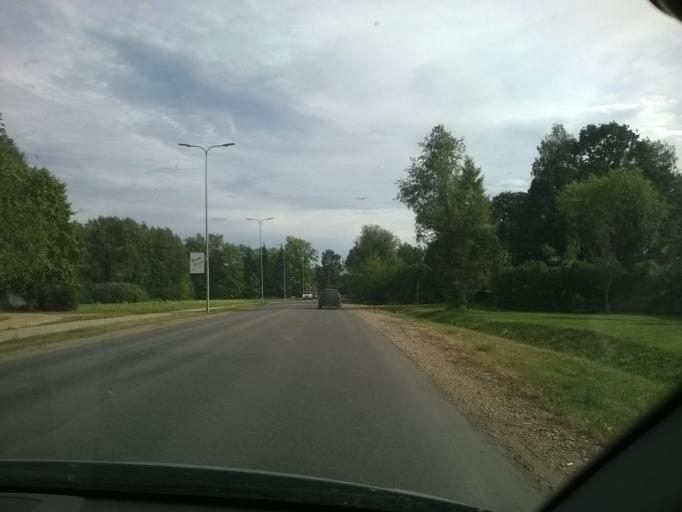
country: EE
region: Vorumaa
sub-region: Voru linn
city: Voru
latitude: 57.8322
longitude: 27.0093
